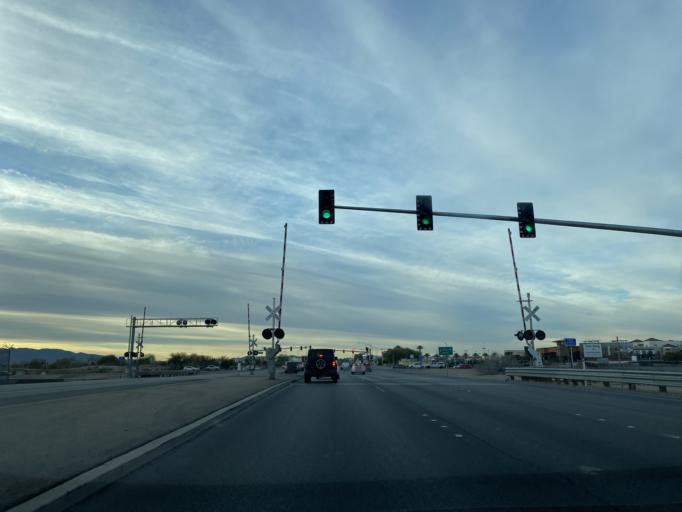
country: US
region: Nevada
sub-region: Clark County
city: Paradise
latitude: 36.0728
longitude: -115.1726
